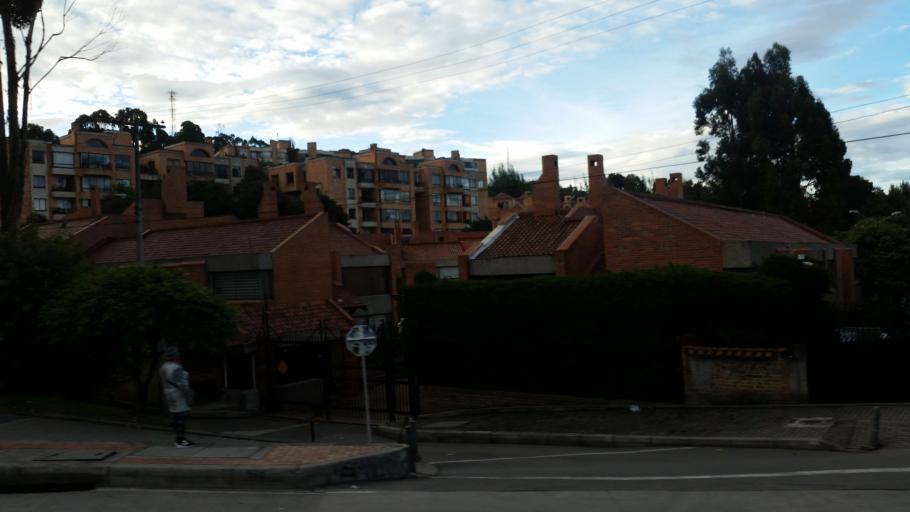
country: CO
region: Cundinamarca
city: Cota
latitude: 4.7331
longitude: -74.0763
